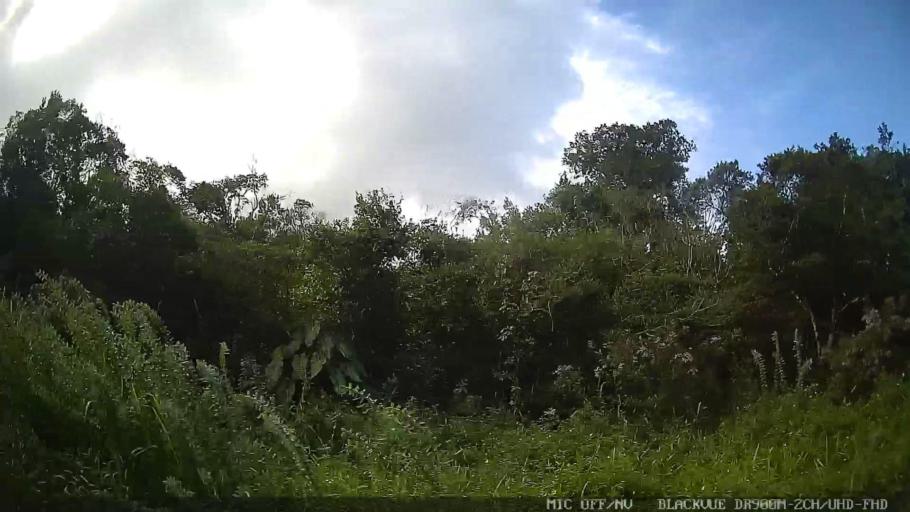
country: BR
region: Sao Paulo
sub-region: Itanhaem
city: Itanhaem
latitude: -24.2194
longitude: -46.9113
